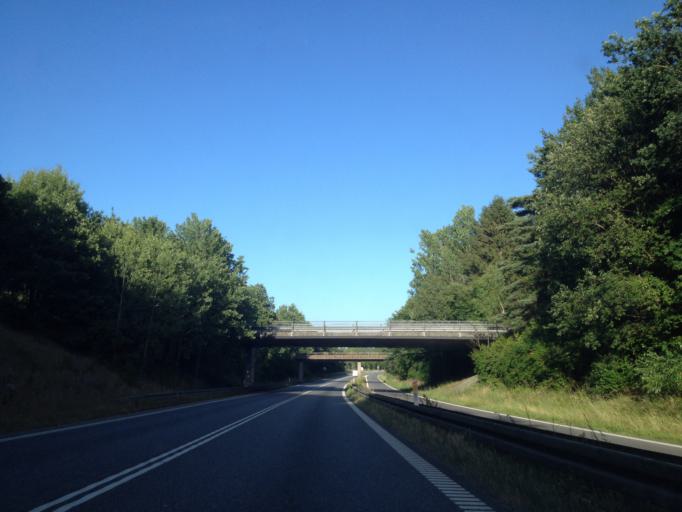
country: DK
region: Capital Region
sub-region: Hillerod Kommune
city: Hillerod
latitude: 55.9530
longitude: 12.3066
